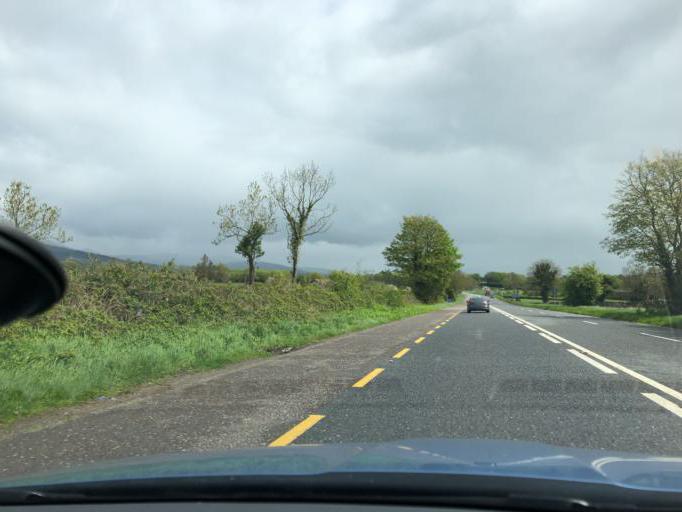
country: IE
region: Munster
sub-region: County Cork
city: Mitchelstown
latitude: 52.2771
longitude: -8.2589
